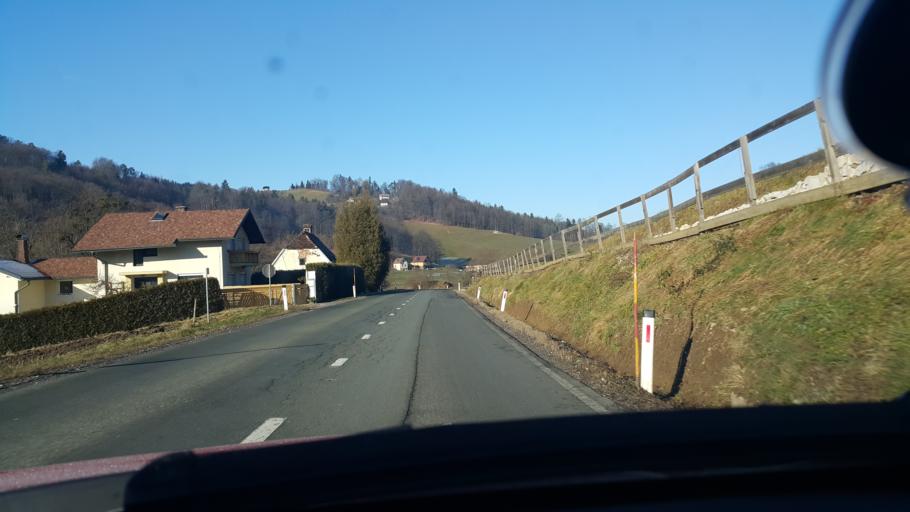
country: SI
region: Kungota
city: Zgornja Kungota
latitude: 46.6197
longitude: 15.6359
